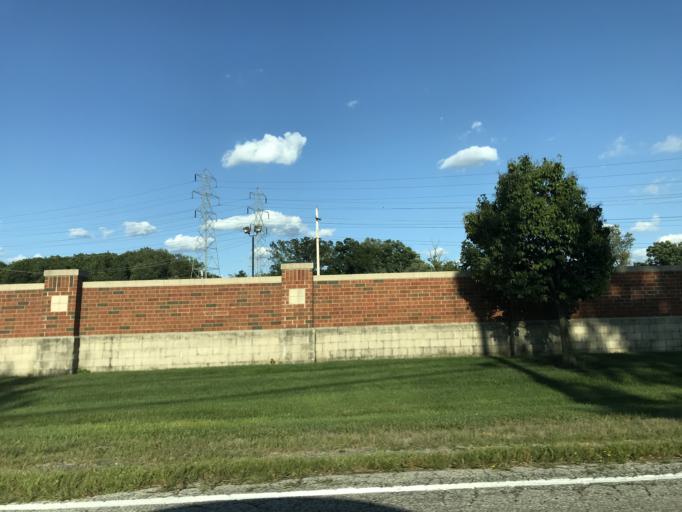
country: US
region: Ohio
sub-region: Cuyahoga County
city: Middleburg Heights
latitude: 41.3646
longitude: -81.8251
